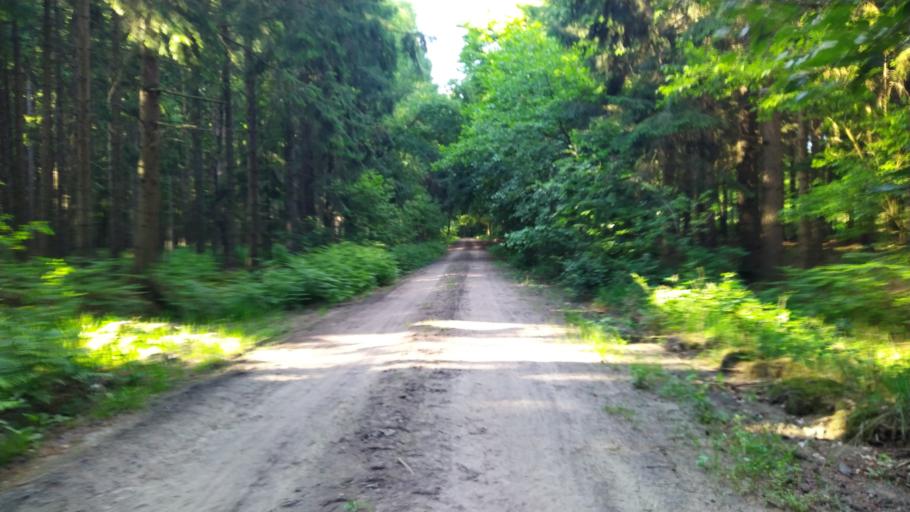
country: DE
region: Lower Saxony
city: Lintig
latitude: 53.5958
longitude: 8.9097
